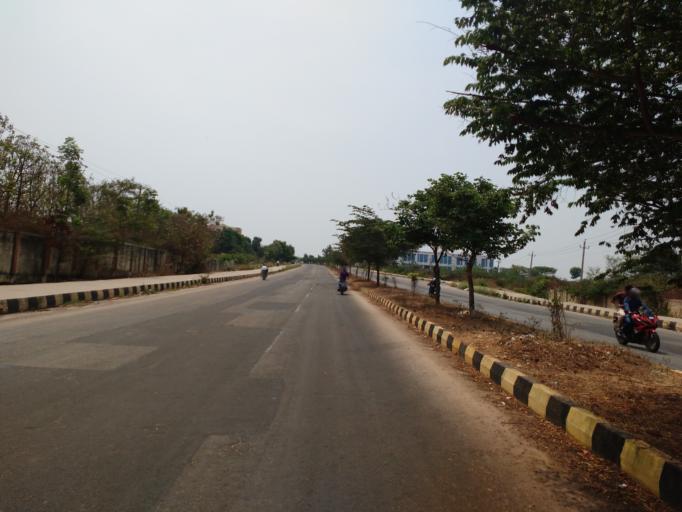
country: IN
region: Karnataka
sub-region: Hassan
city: Hassan
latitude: 13.0142
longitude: 76.1190
